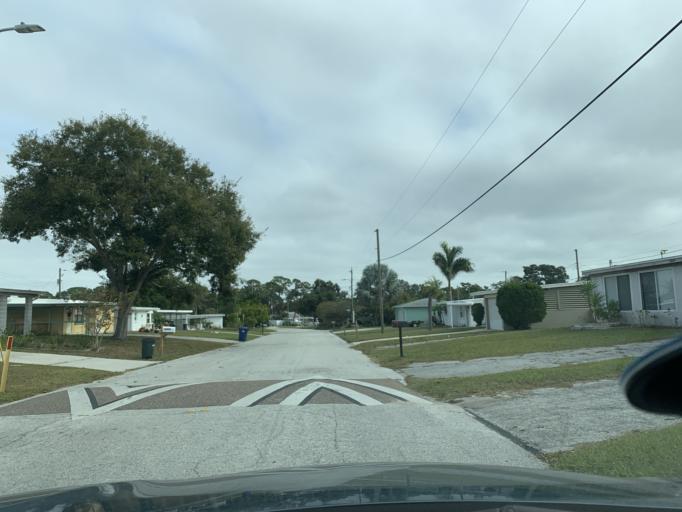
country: US
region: Florida
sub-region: Pinellas County
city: Ridgecrest
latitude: 27.8815
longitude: -82.7843
